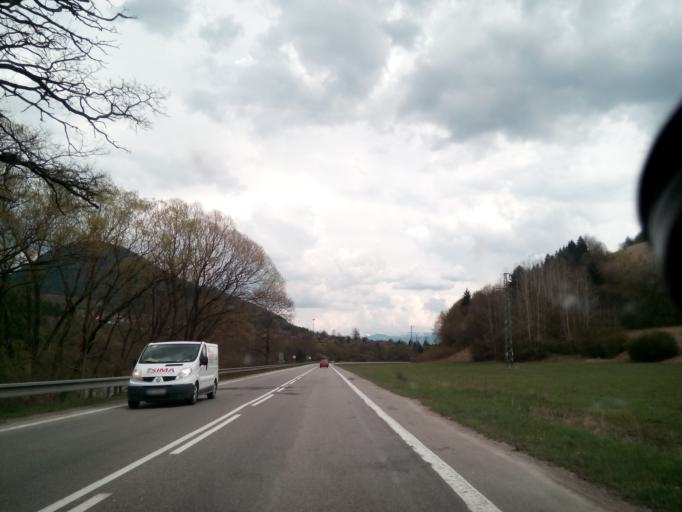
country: SK
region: Zilinsky
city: Ruzomberok
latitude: 49.1079
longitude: 19.2349
